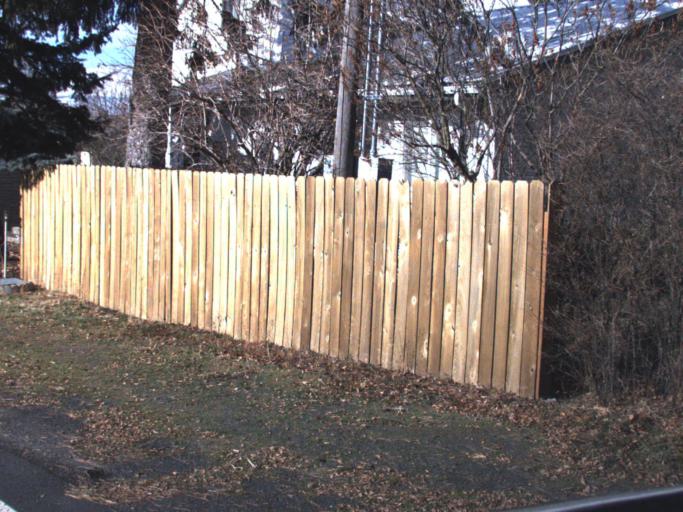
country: US
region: Idaho
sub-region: Latah County
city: Moscow
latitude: 46.9114
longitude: -117.0856
